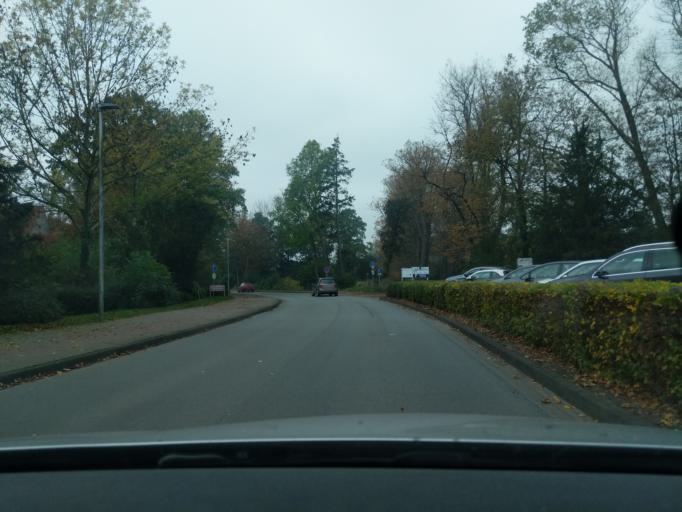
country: DE
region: Lower Saxony
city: Otterndorf
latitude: 53.8132
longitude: 8.8879
